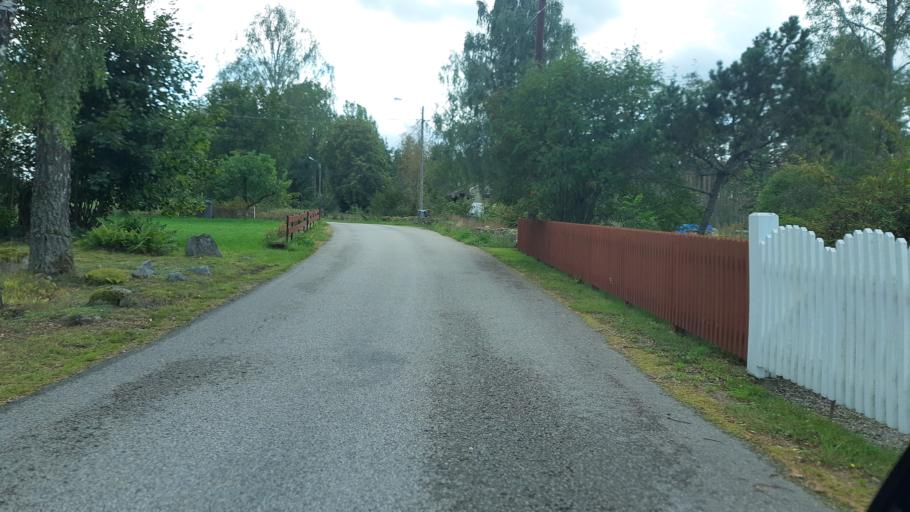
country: SE
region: Kronoberg
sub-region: Tingsryds Kommun
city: Tingsryd
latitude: 56.5023
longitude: 15.1548
